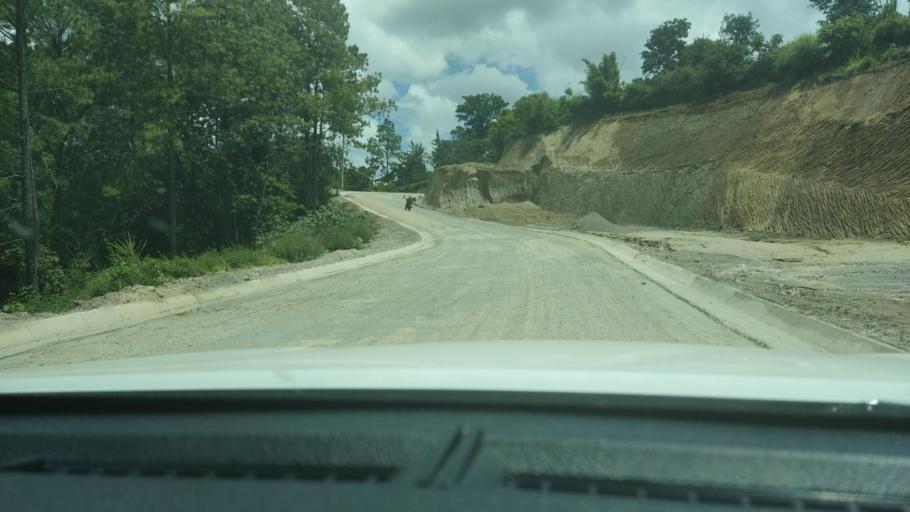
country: GT
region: Chimaltenango
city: San Martin Jilotepeque
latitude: 14.7905
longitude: -90.8028
